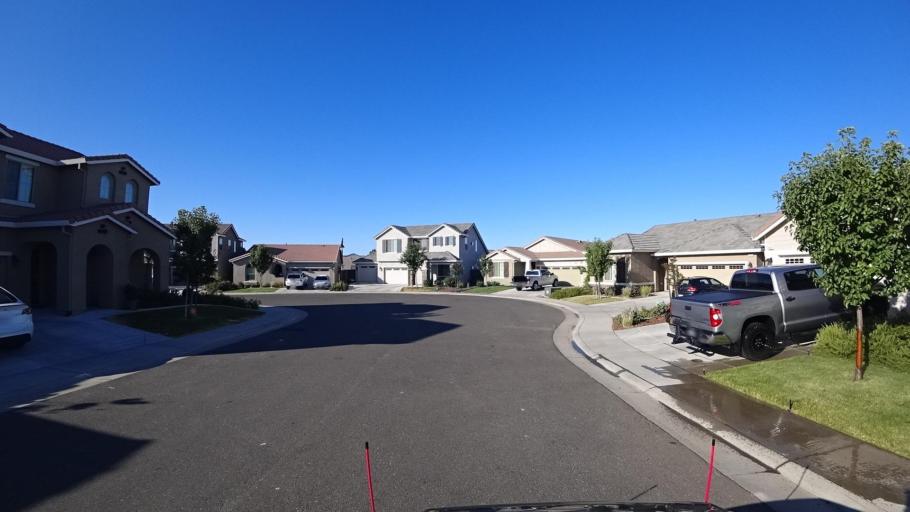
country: US
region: California
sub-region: Placer County
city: Rocklin
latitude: 38.8267
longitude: -121.2665
